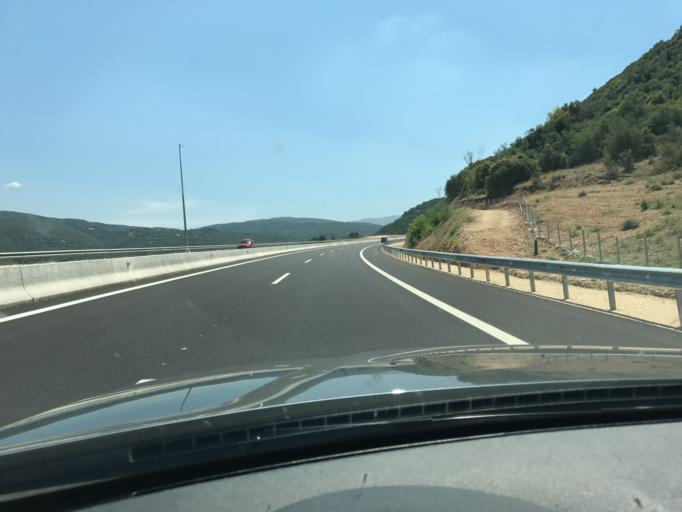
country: GR
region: Epirus
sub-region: Nomos Ioanninon
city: Agia Kyriaki
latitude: 39.5161
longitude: 20.8857
